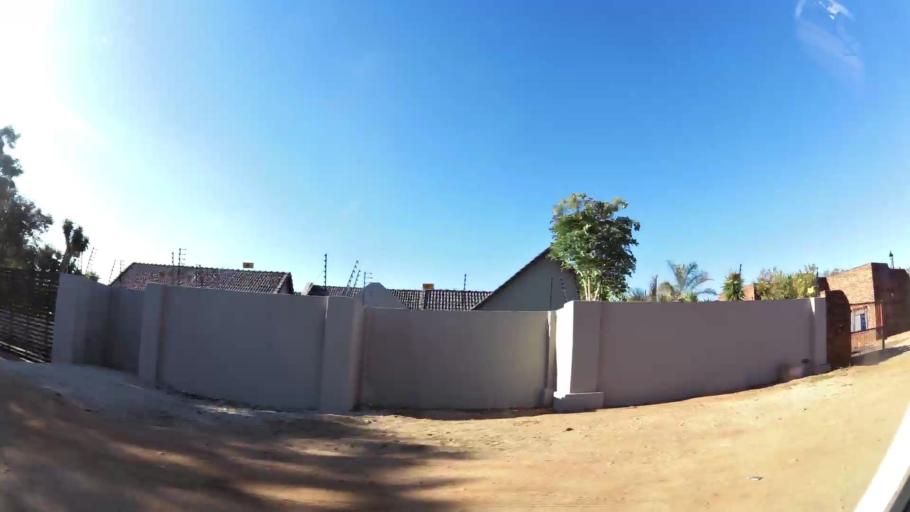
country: ZA
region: Limpopo
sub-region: Capricorn District Municipality
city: Polokwane
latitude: -23.8851
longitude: 29.4862
